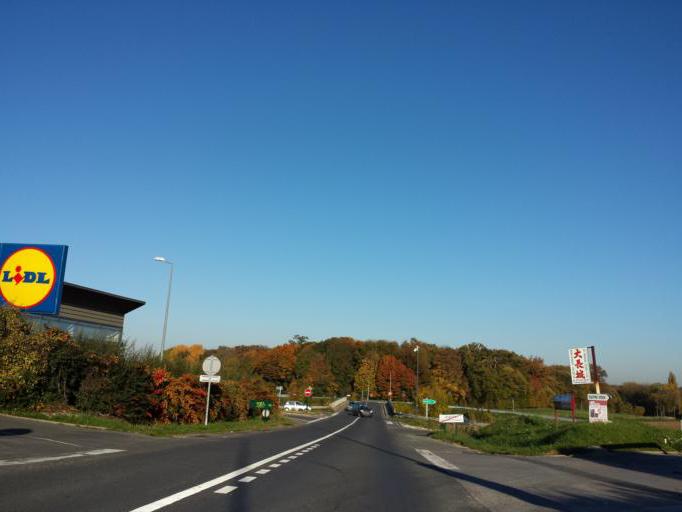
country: FR
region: Ile-de-France
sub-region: Departement du Val-d'Oise
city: Saint-Brice-sous-Foret
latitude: 49.0188
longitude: 2.3504
